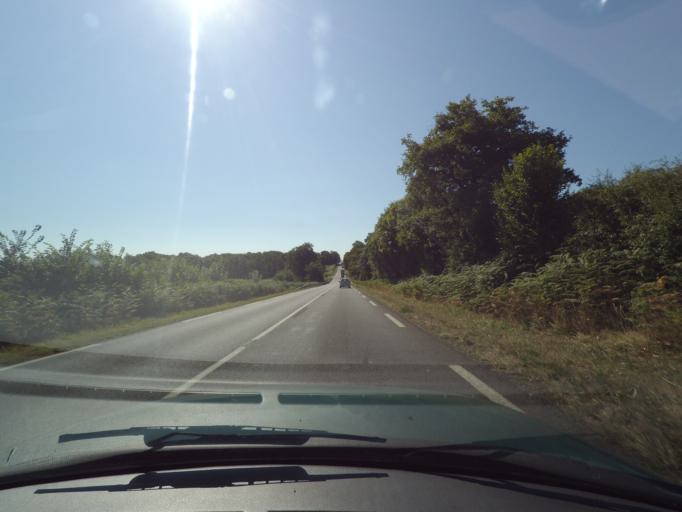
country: FR
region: Limousin
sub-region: Departement de la Haute-Vienne
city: Bussiere-Poitevine
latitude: 46.1798
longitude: 0.9400
